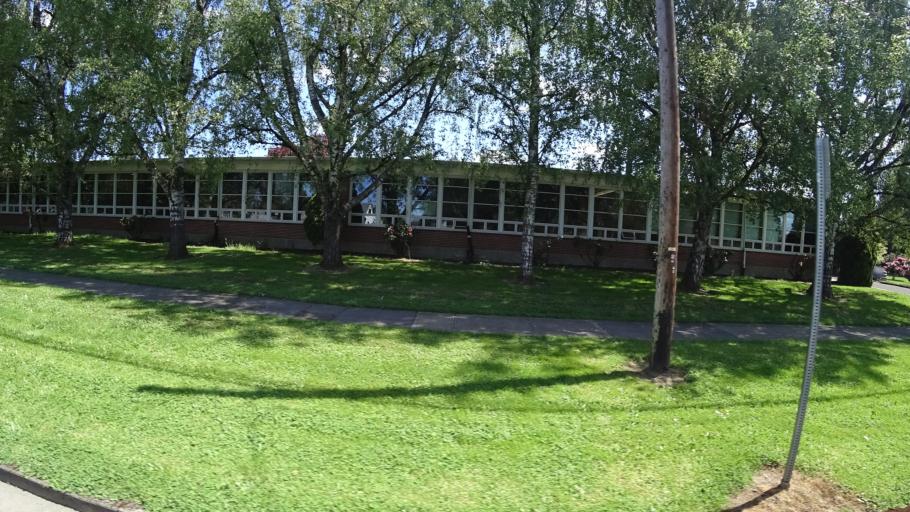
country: US
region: Oregon
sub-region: Washington County
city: Hillsboro
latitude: 45.5179
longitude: -122.9845
